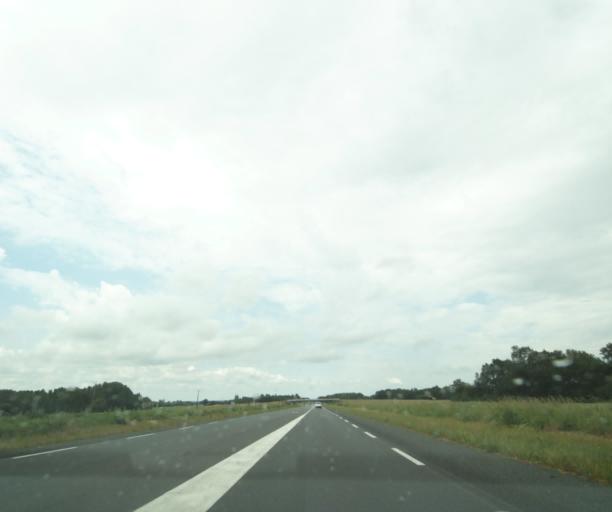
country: FR
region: Poitou-Charentes
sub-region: Departement des Deux-Sevres
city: Louzy
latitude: 47.0647
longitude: -0.1803
